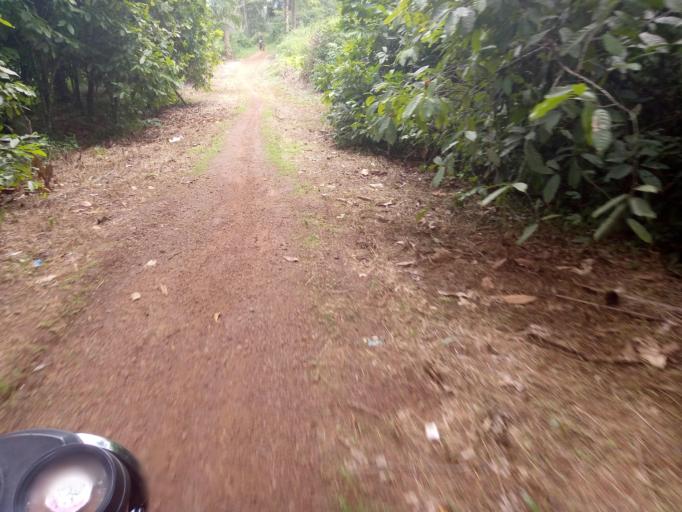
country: SL
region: Eastern Province
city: Buedu
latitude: 8.4807
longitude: -10.3288
